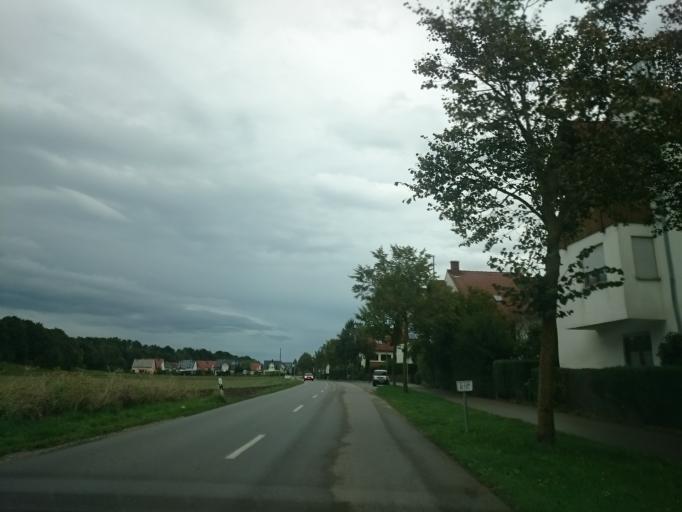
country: DE
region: Bavaria
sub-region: Swabia
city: Untermeitingen
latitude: 48.1663
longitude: 10.8091
